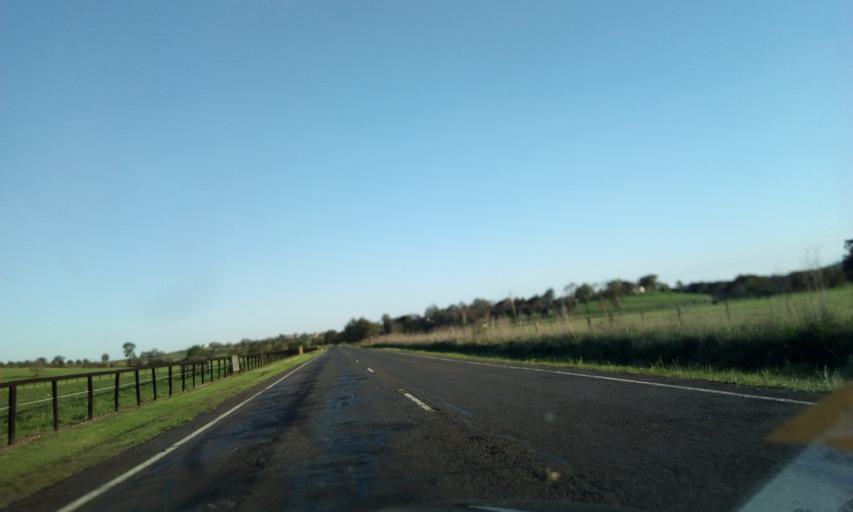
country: AU
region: New South Wales
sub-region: Wollondilly
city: Douglas Park
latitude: -34.1356
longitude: 150.7109
